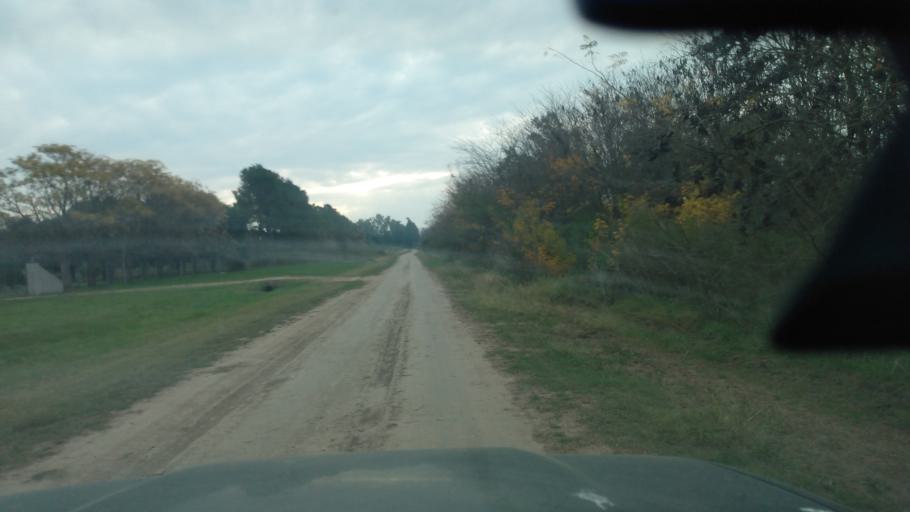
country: AR
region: Buenos Aires
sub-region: Partido de Lujan
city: Lujan
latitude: -34.5629
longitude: -59.1539
